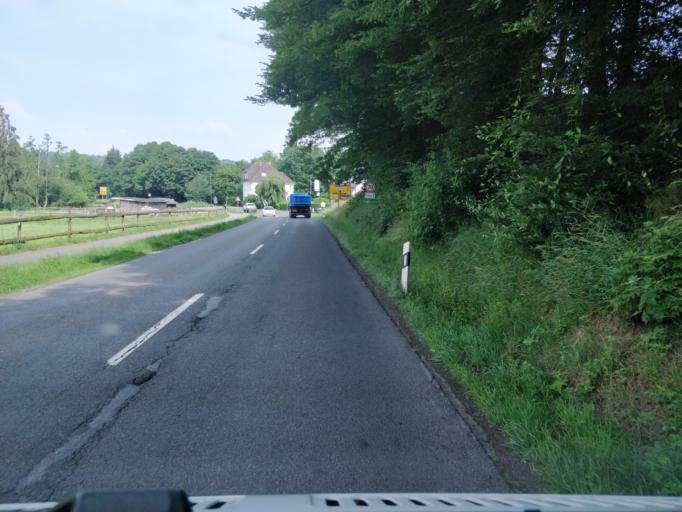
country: DE
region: North Rhine-Westphalia
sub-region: Regierungsbezirk Koln
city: Numbrecht
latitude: 50.9213
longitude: 7.5786
